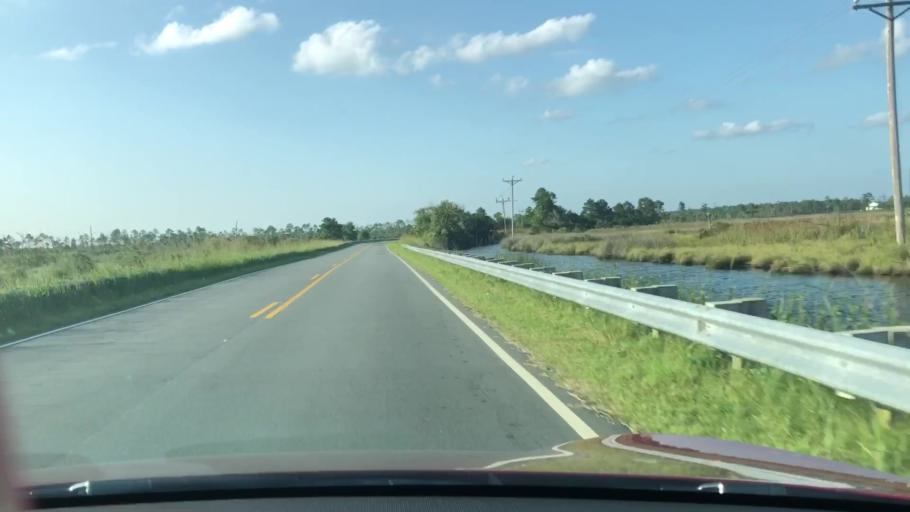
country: US
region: North Carolina
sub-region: Dare County
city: Wanchese
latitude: 35.6877
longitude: -75.7808
